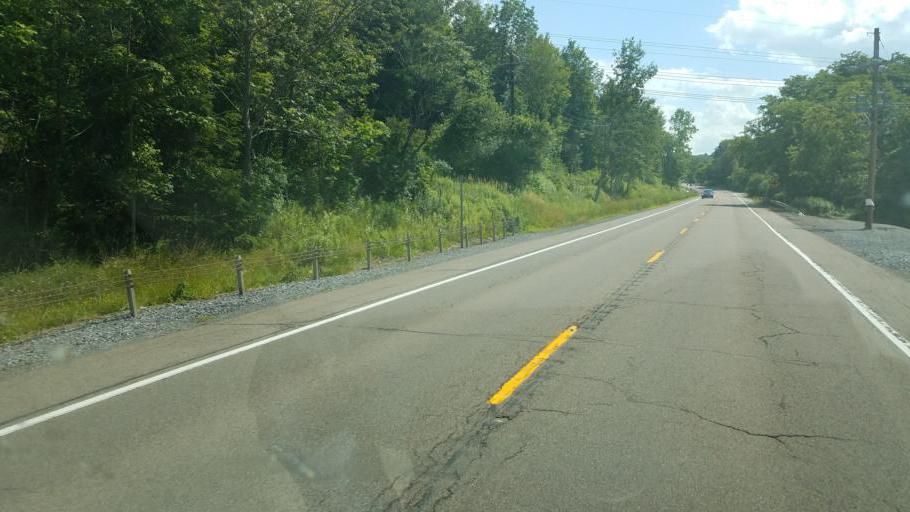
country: US
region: New York
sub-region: Steuben County
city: Sylvan Beach
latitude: 42.4939
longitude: -77.1178
